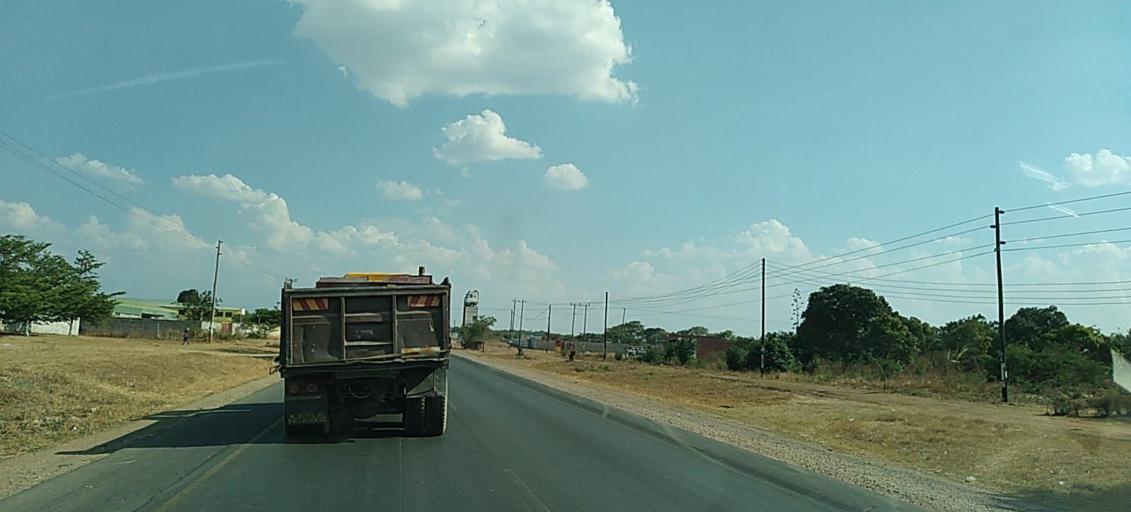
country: ZM
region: Lusaka
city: Lusaka
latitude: -15.2377
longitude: 28.2571
